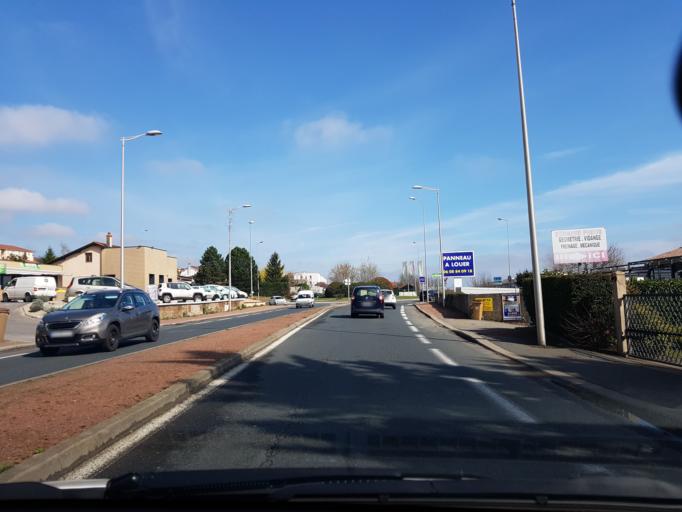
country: FR
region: Rhone-Alpes
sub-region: Departement du Rhone
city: Villefranche-sur-Saone
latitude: 45.9721
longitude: 4.7171
